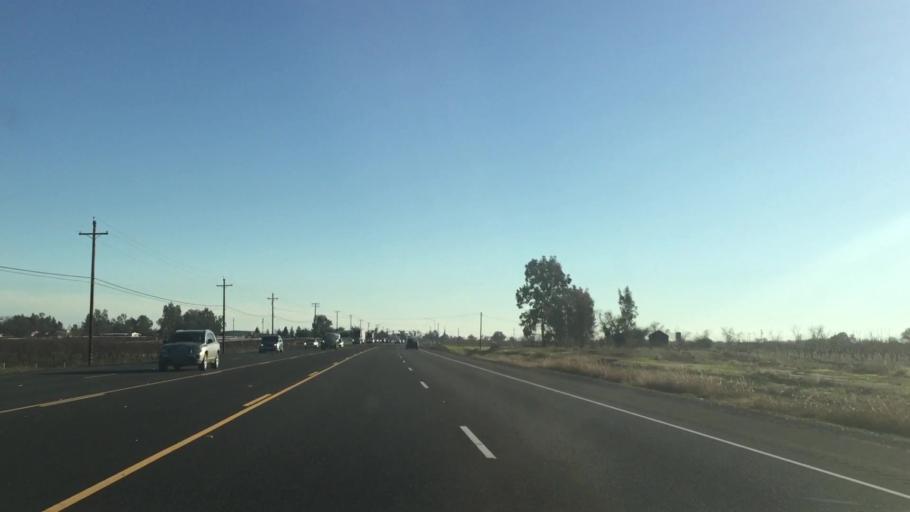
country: US
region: California
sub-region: Butte County
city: Gridley
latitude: 39.3696
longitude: -121.6100
